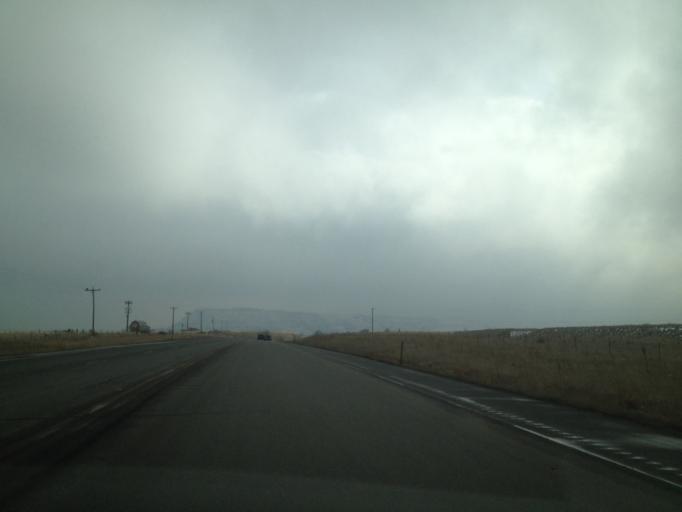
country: US
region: Colorado
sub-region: Jefferson County
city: Golden
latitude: 39.8358
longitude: -105.2298
